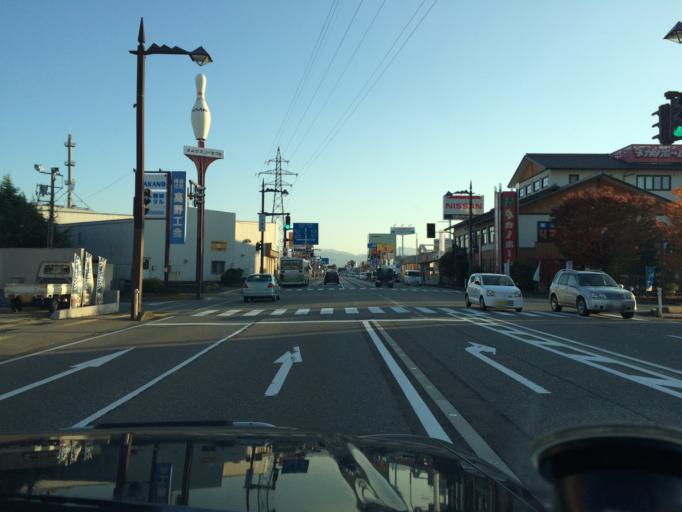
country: JP
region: Toyama
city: Toyama-shi
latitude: 36.6704
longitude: 137.2104
